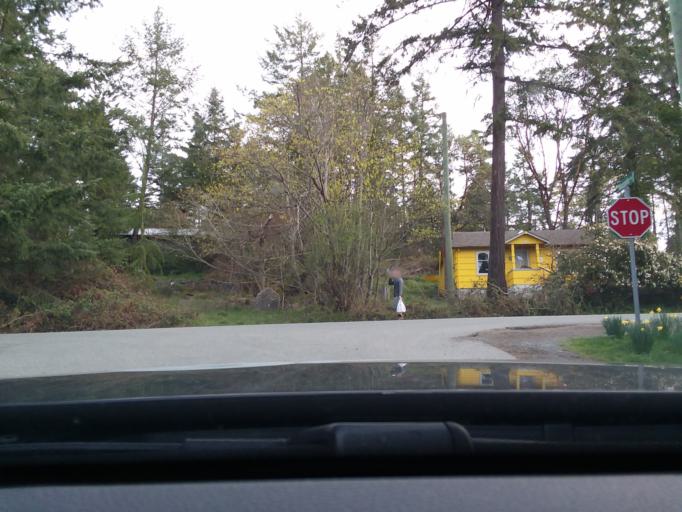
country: CA
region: British Columbia
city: North Saanich
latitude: 48.8793
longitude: -123.3202
